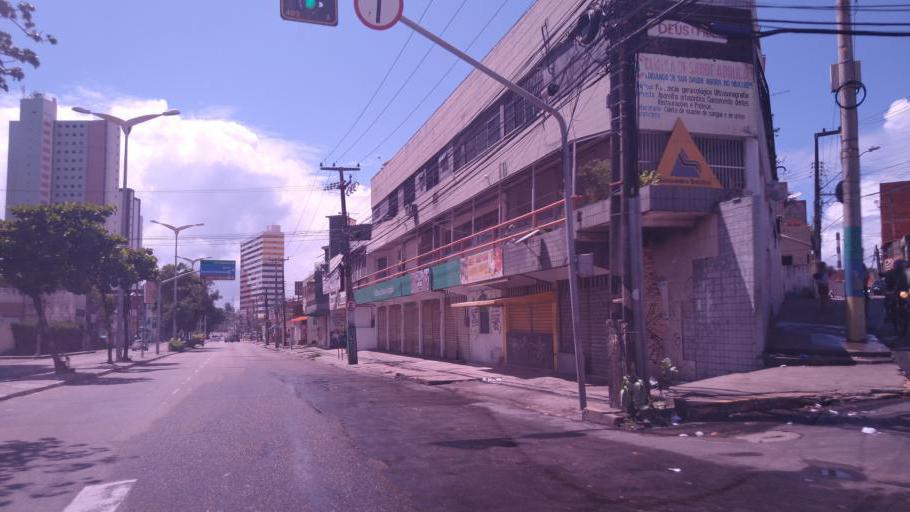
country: BR
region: Ceara
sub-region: Fortaleza
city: Fortaleza
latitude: -3.7241
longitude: -38.4817
